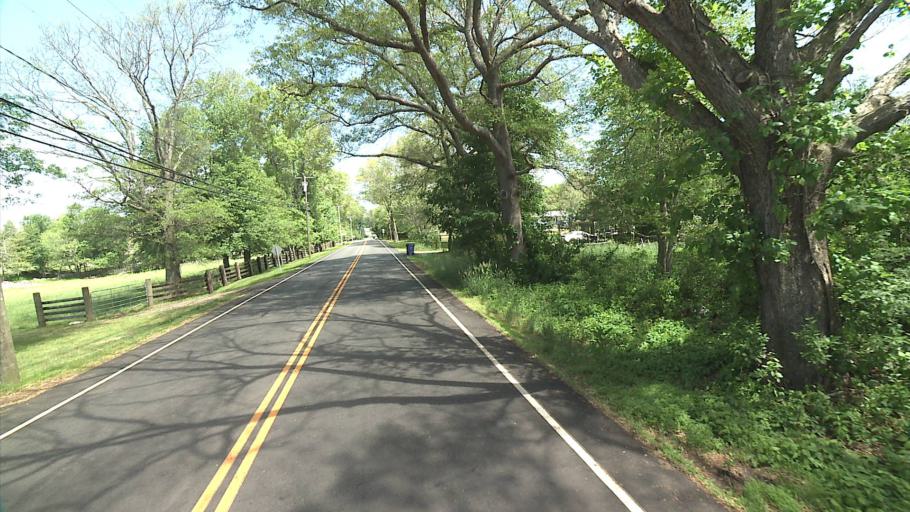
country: US
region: Connecticut
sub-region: Windham County
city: Moosup
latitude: 41.6853
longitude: -71.8492
